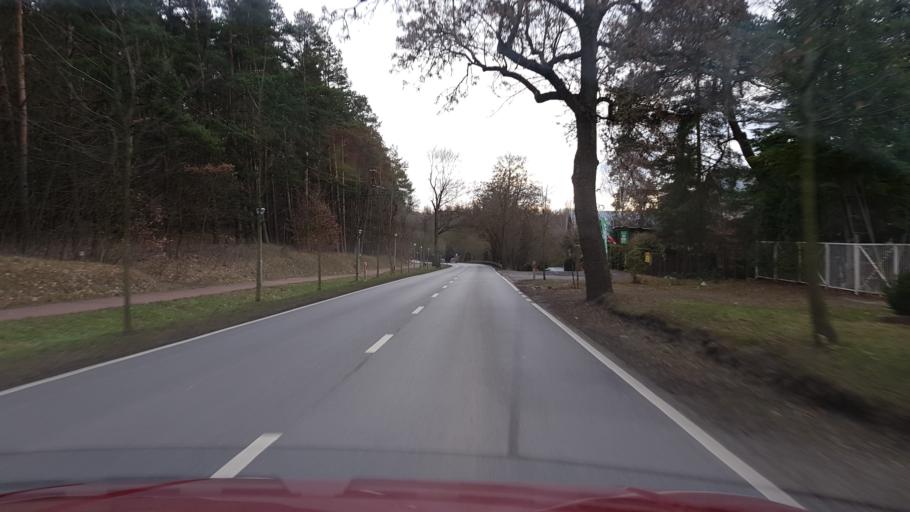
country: PL
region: West Pomeranian Voivodeship
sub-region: Powiat policki
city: Dobra
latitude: 53.4913
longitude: 14.4810
